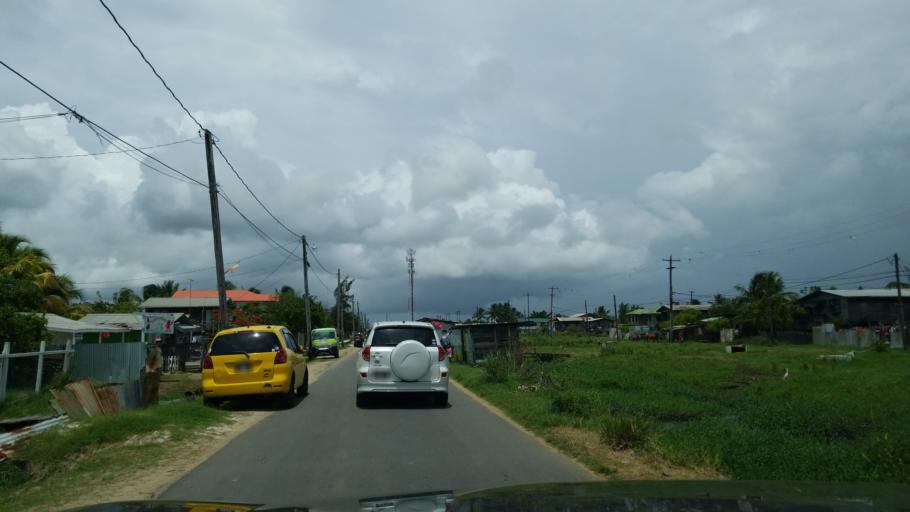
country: GY
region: Demerara-Mahaica
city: Georgetown
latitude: 6.8071
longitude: -58.1216
